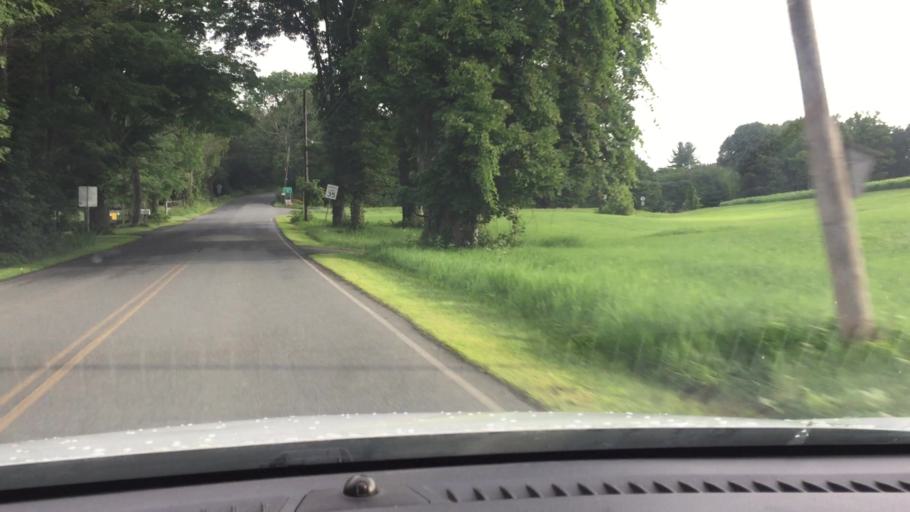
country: US
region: Massachusetts
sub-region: Hampshire County
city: Chesterfield
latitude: 42.2740
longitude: -72.9137
